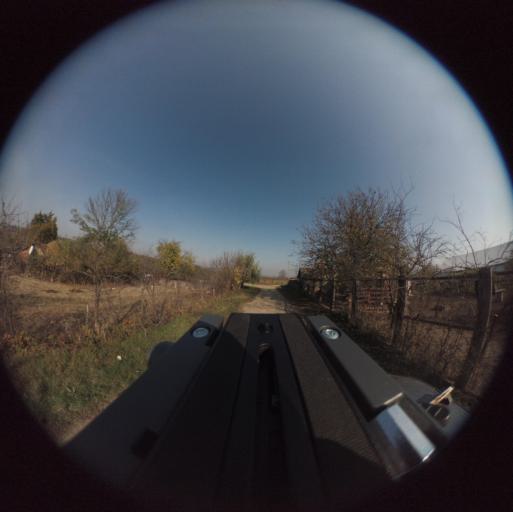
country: RO
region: Vaslui
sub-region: Comuna Dumesti
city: Dumesti
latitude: 46.8312
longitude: 27.2641
